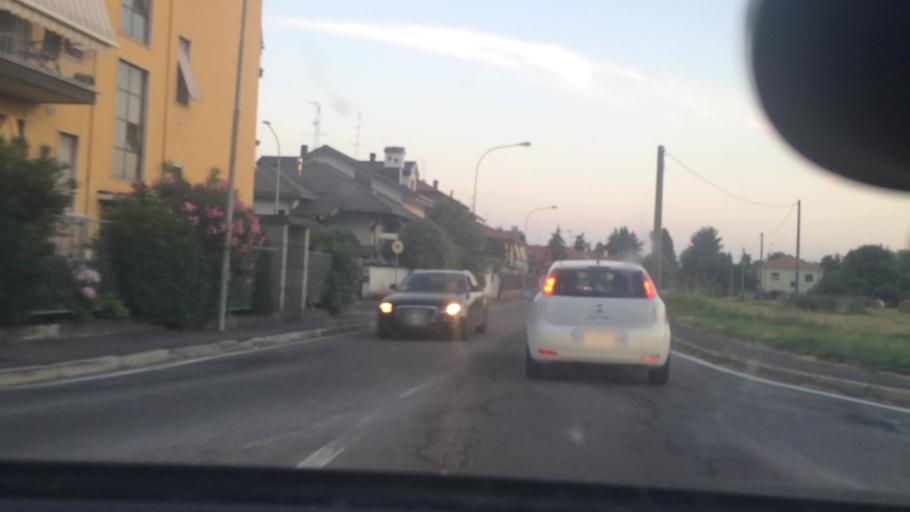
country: IT
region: Lombardy
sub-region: Citta metropolitana di Milano
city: Parabiago
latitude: 45.5472
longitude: 8.9410
